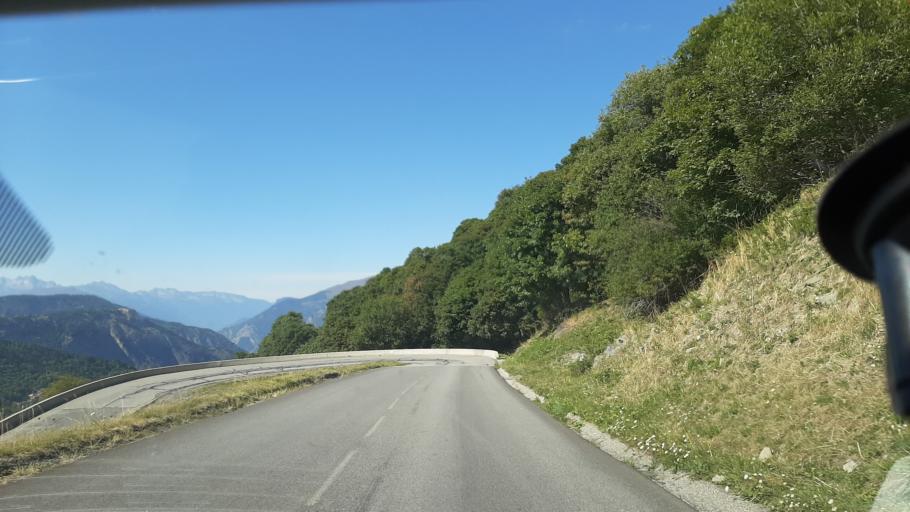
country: FR
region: Rhone-Alpes
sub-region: Departement de la Savoie
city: Saint-Michel-de-Maurienne
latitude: 45.1816
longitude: 6.4855
